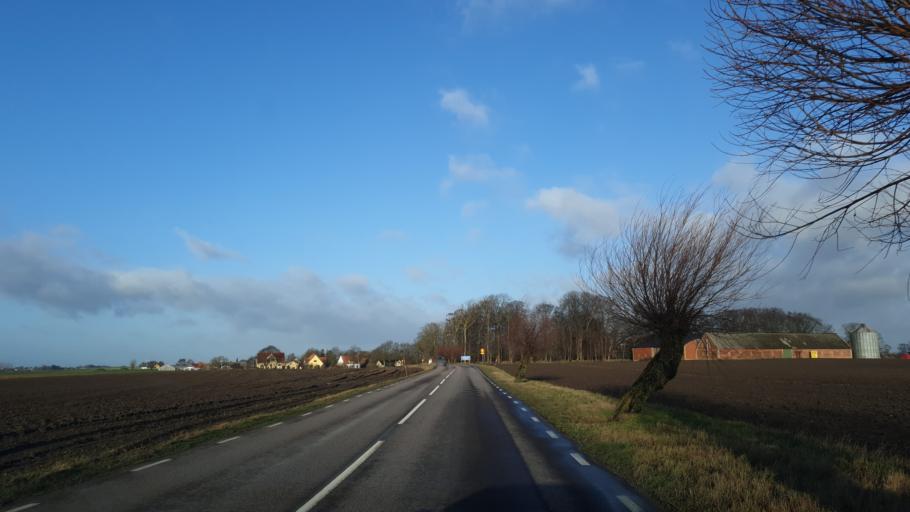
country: SE
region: Skane
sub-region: Vellinge Kommun
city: Vellinge
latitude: 55.4961
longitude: 13.0280
